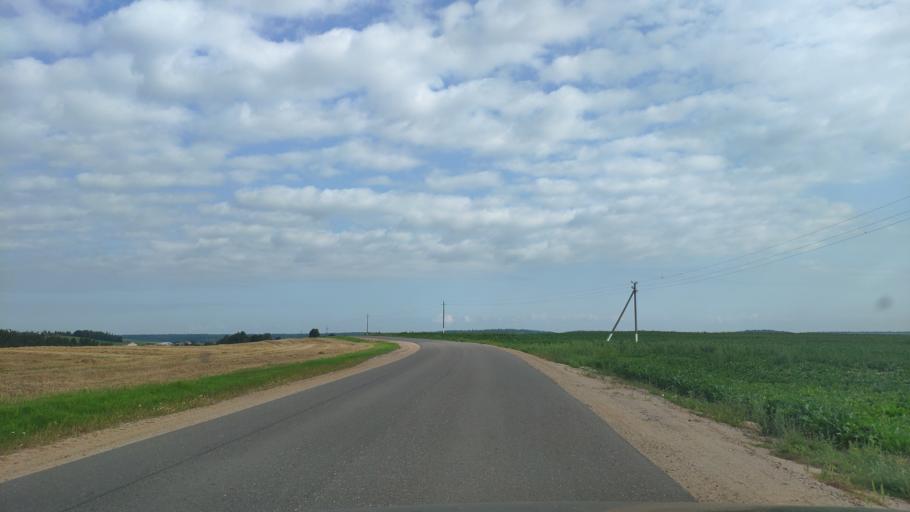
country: BY
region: Minsk
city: Khatsyezhyna
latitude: 53.8446
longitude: 27.3135
